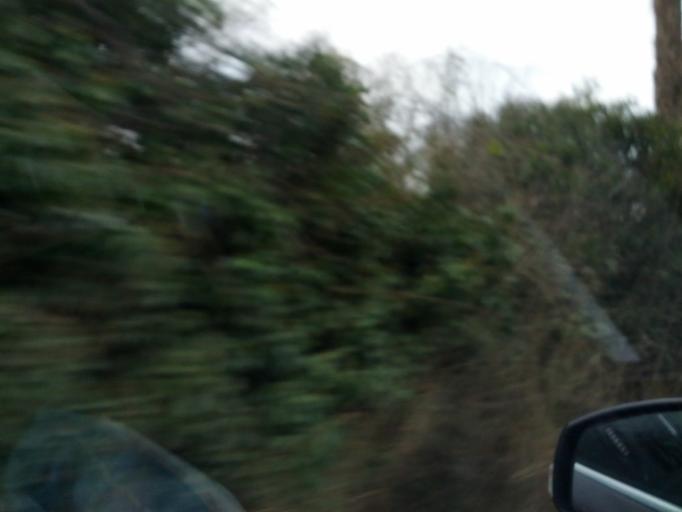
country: IE
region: Connaught
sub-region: County Galway
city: Oranmore
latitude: 53.2213
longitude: -8.8392
